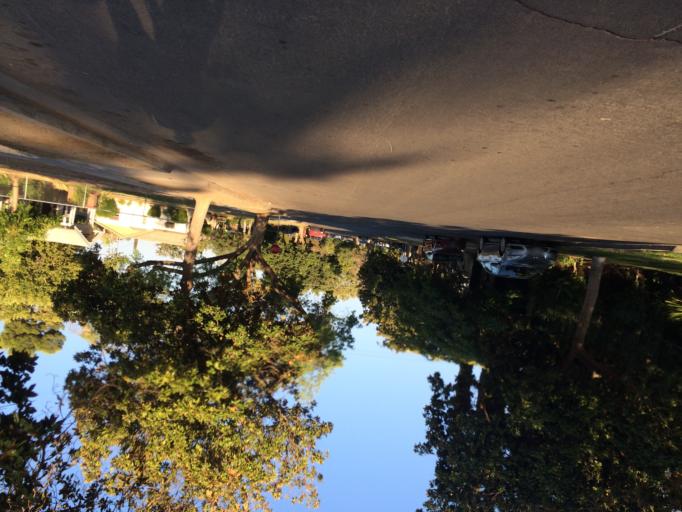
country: US
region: California
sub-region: Fresno County
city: Fresno
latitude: 36.7477
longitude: -119.7439
